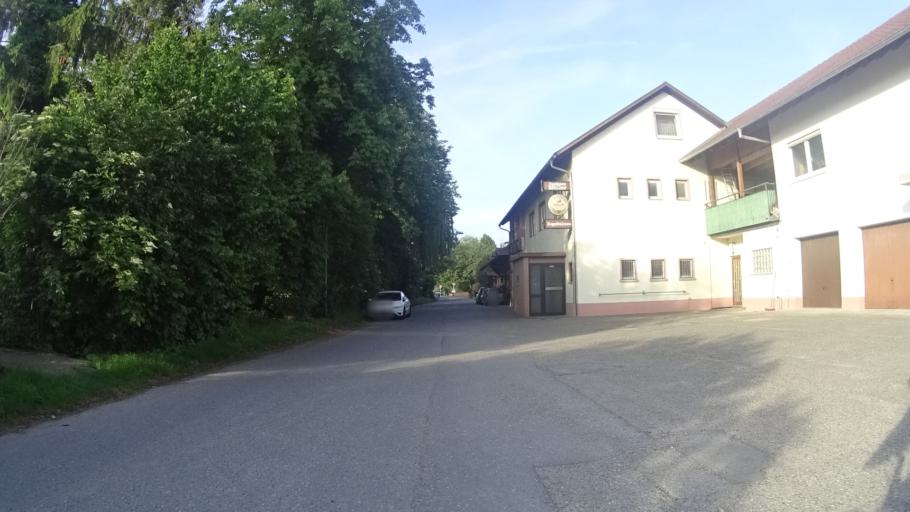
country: DE
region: Baden-Wuerttemberg
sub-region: Freiburg Region
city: Hartheim
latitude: 47.9380
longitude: 7.6464
